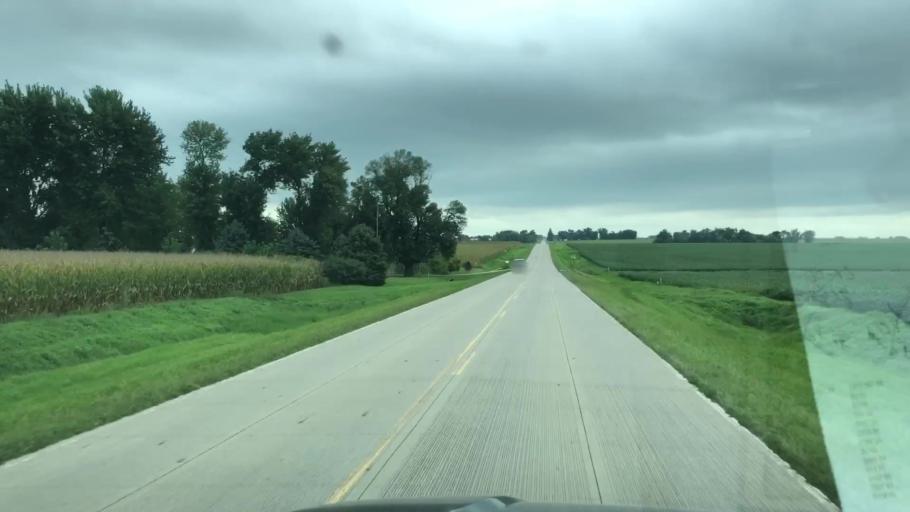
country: US
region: Iowa
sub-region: O'Brien County
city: Sheldon
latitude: 43.1209
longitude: -95.9789
